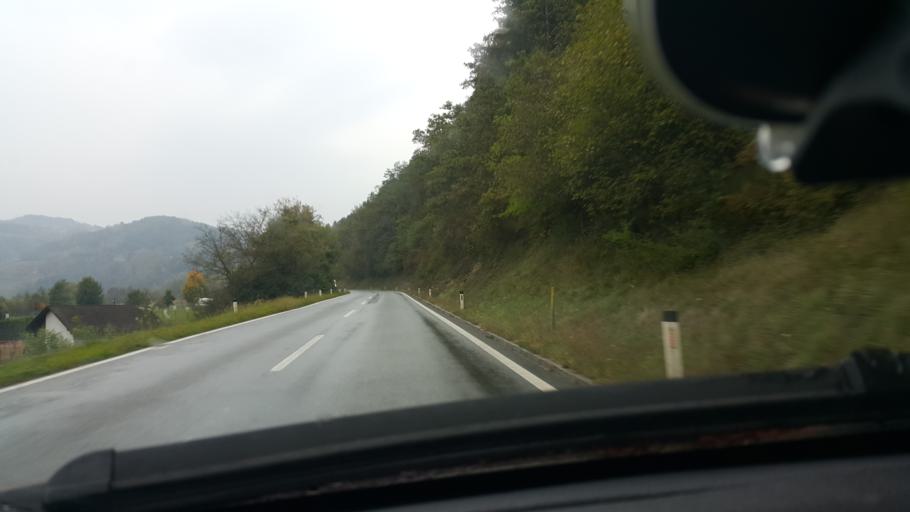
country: AT
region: Carinthia
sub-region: Politischer Bezirk Wolfsberg
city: Lavamund
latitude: 46.6474
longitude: 14.9352
